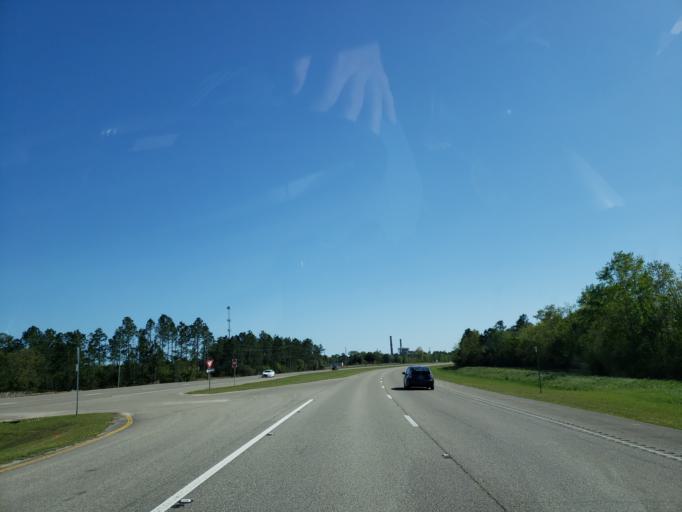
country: US
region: Mississippi
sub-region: Harrison County
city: West Gulfport
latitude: 30.4621
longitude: -89.0268
